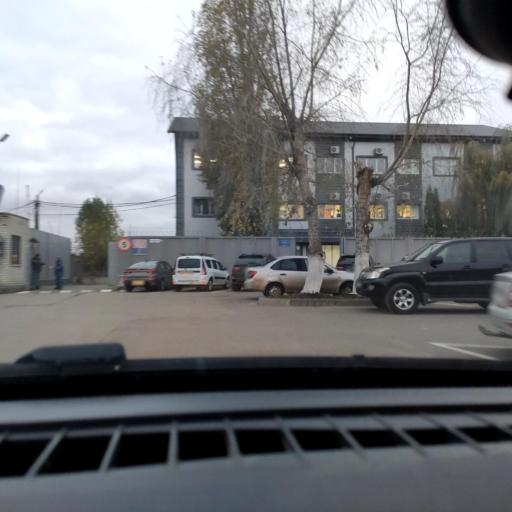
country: RU
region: Voronezj
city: Podgornoye
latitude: 51.8014
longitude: 39.1973
